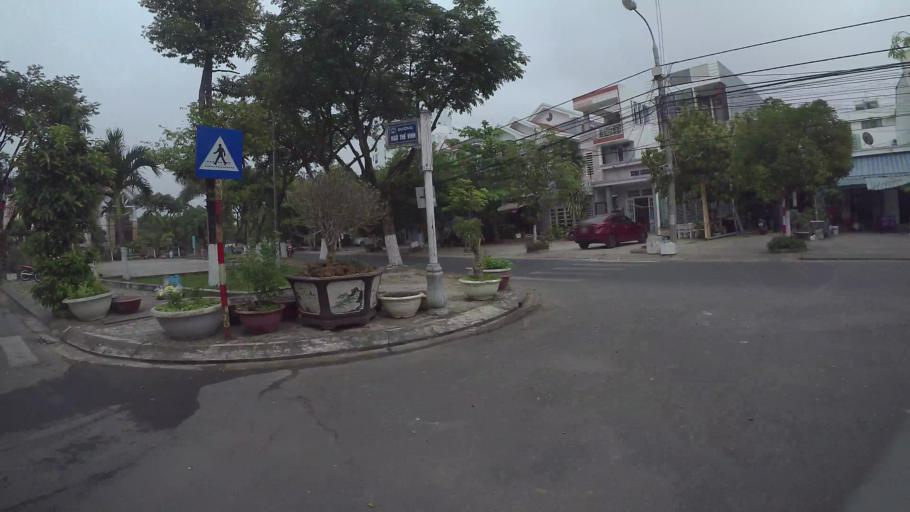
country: VN
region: Da Nang
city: Cam Le
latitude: 16.0406
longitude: 108.2096
